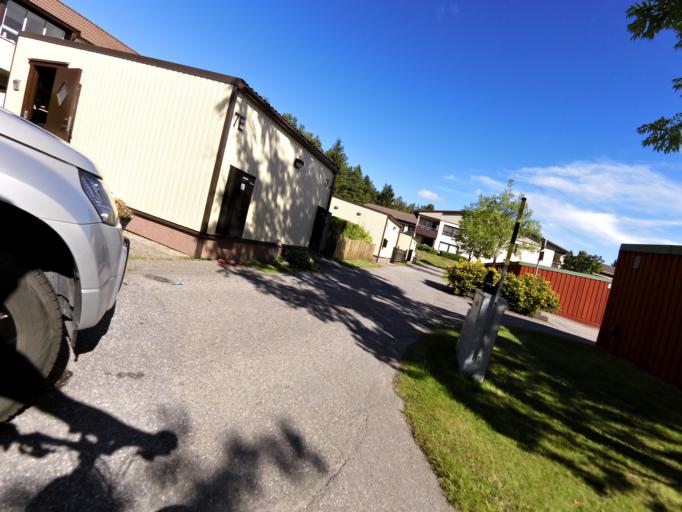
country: SE
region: Gaevleborg
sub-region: Gavle Kommun
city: Gavle
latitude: 60.6652
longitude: 17.2113
